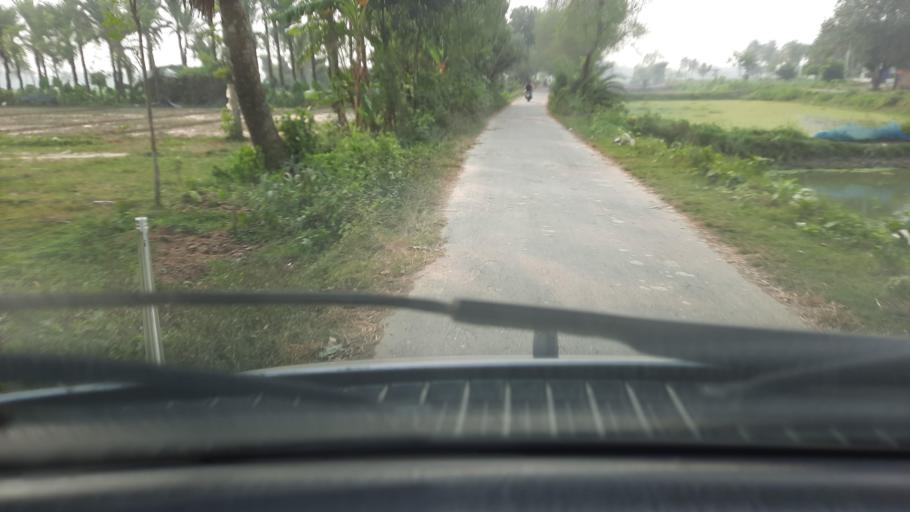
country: BD
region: Khulna
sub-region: Chuadanga
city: Nowlamary
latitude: 23.6012
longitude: 88.8533
